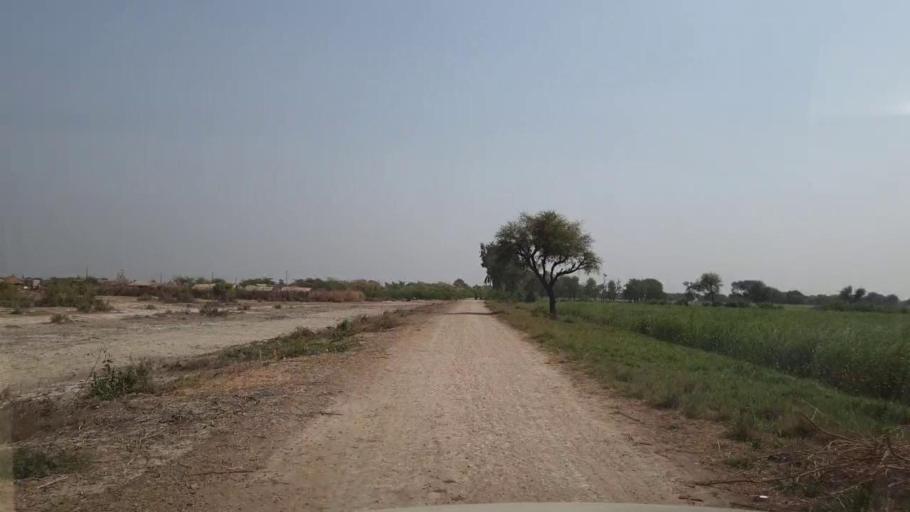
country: PK
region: Sindh
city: Dhoro Naro
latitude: 25.4580
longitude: 69.6288
